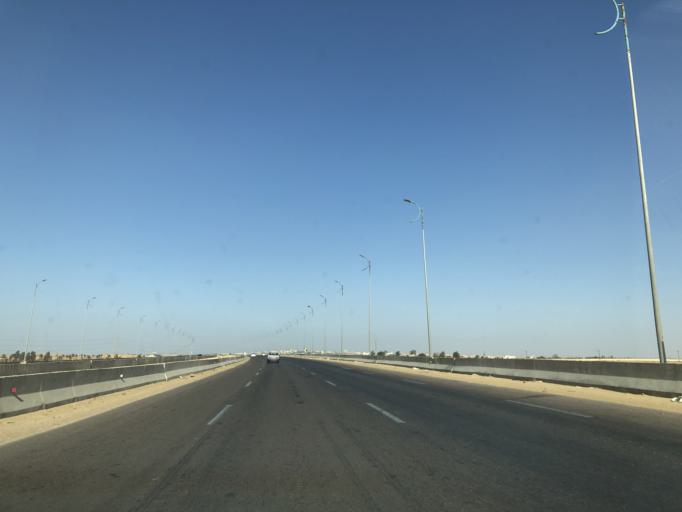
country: EG
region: Al Jizah
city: Awsim
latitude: 30.0680
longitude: 30.9013
